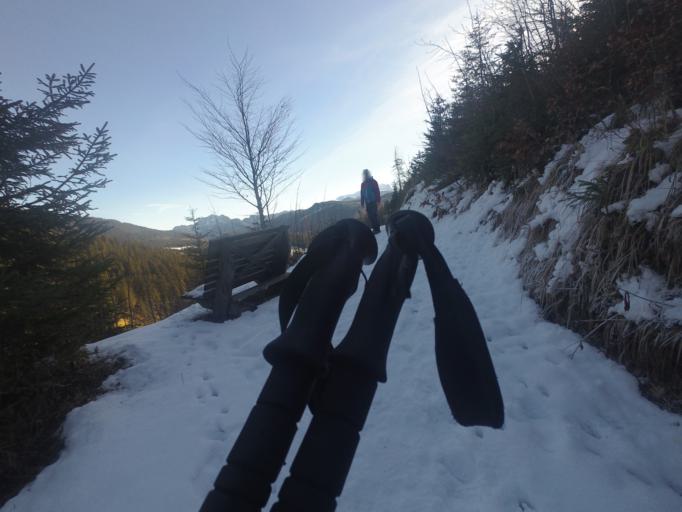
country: AT
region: Salzburg
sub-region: Politischer Bezirk Hallein
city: Abtenau
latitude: 47.6011
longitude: 13.4579
